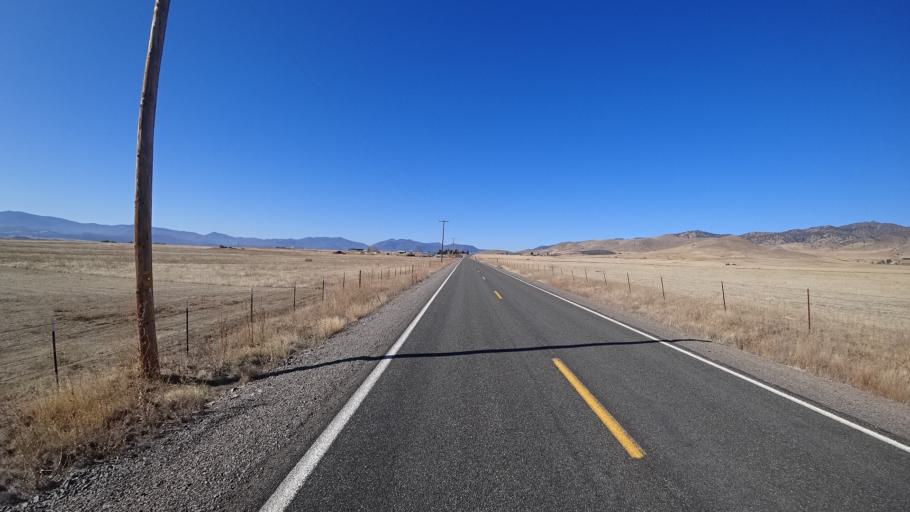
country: US
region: California
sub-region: Siskiyou County
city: Montague
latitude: 41.7706
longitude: -122.5069
